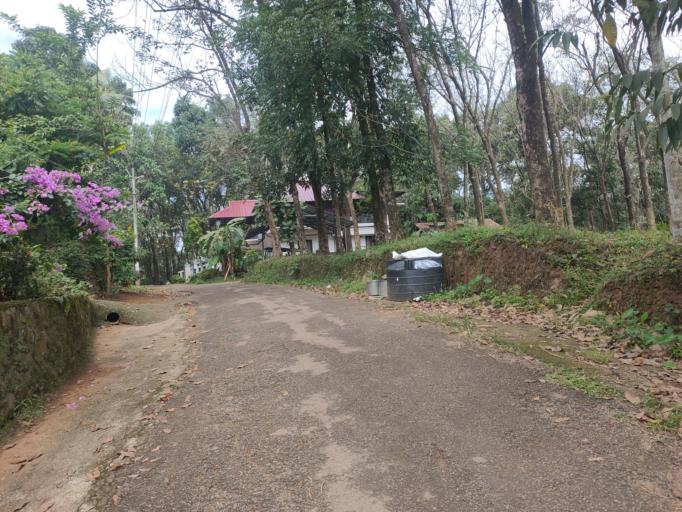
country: IN
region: Kerala
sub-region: Ernakulam
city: Kotamangalam
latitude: 10.0108
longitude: 76.6464
